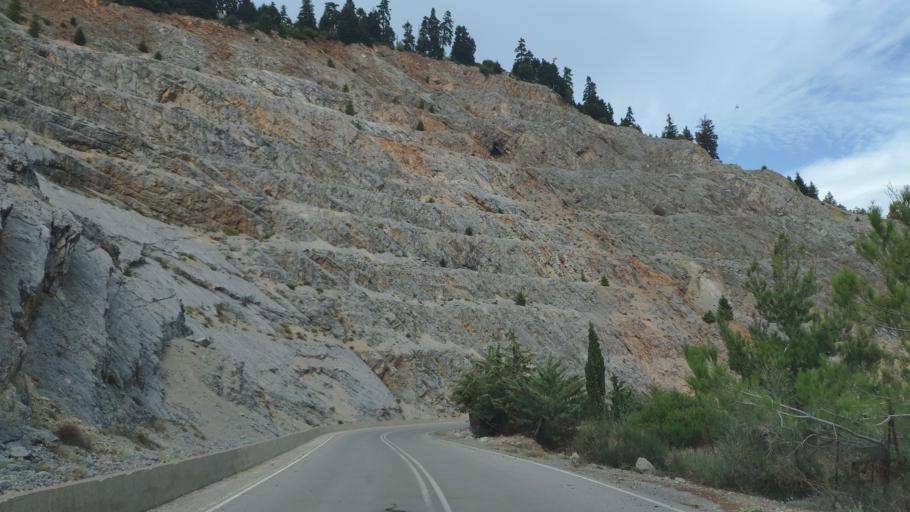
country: GR
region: Central Greece
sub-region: Nomos Fokidos
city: Amfissa
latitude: 38.6534
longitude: 22.3819
